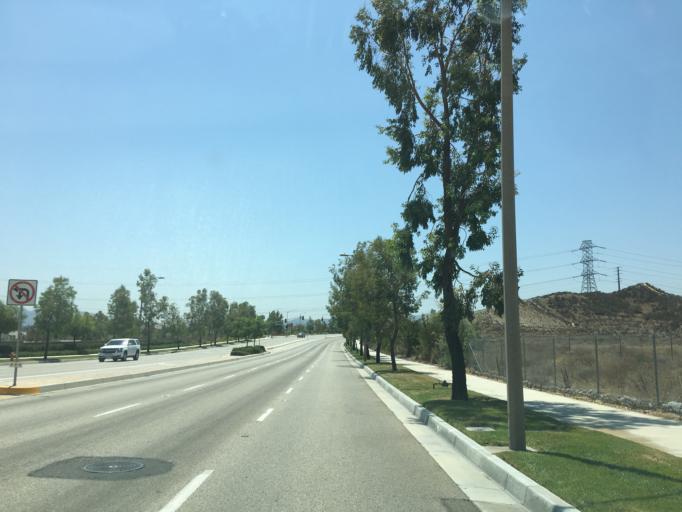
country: US
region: California
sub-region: Los Angeles County
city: Valencia
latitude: 34.4537
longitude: -118.5662
